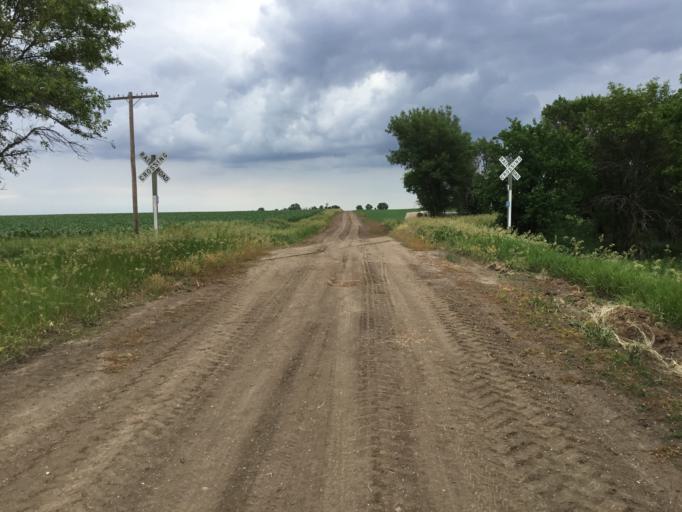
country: US
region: Kansas
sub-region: Republic County
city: Belleville
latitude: 39.8714
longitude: -97.5761
